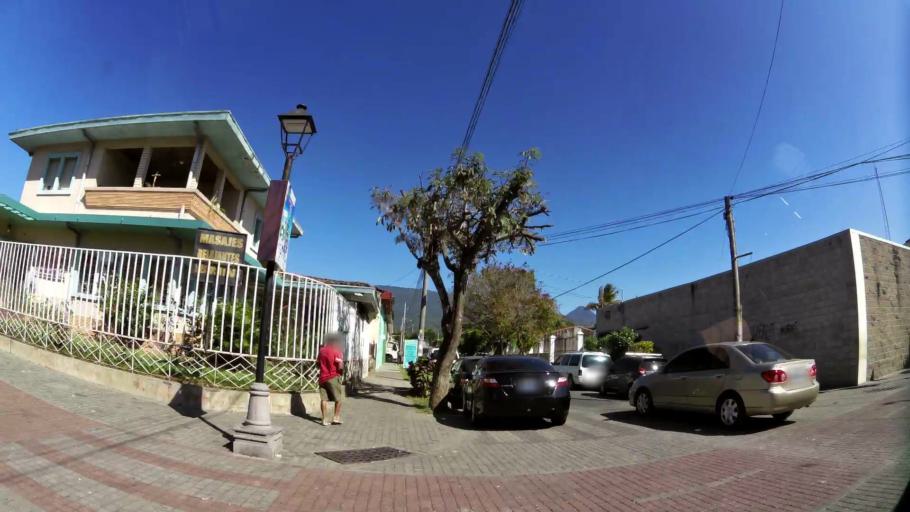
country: SV
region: La Libertad
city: Santa Tecla
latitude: 13.6755
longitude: -89.2902
